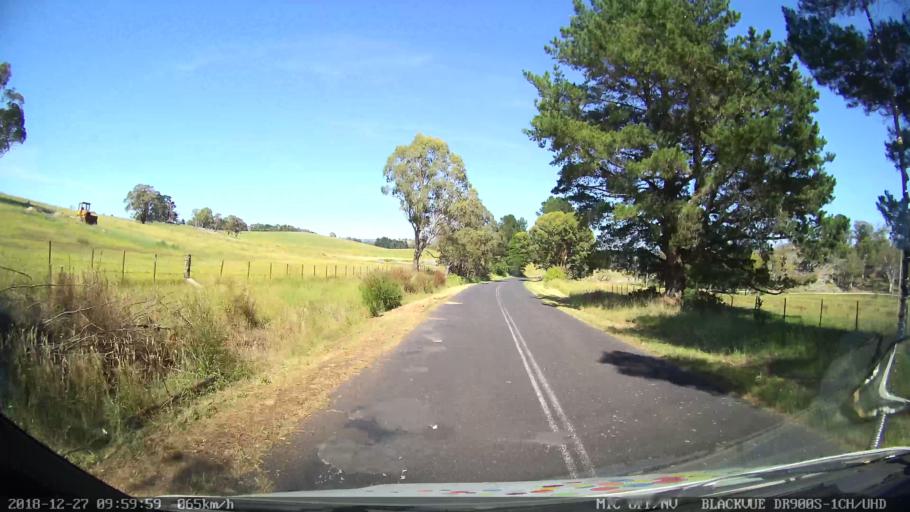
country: AU
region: New South Wales
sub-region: Lithgow
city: Portland
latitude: -33.4360
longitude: 149.9453
